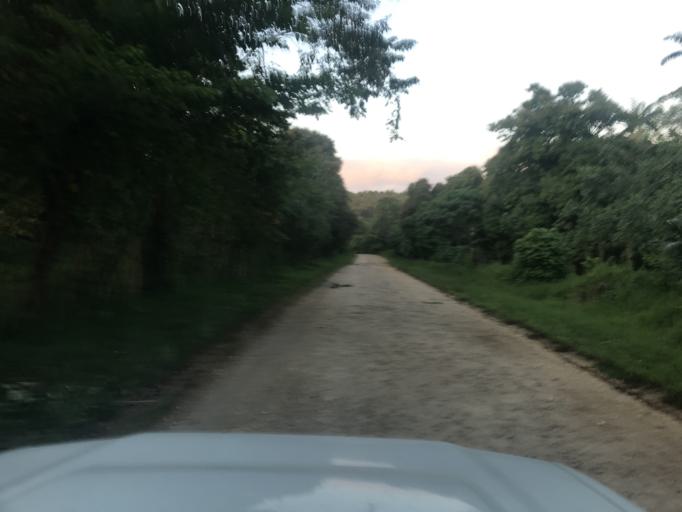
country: VU
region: Sanma
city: Luganville
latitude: -15.5597
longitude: 166.9655
